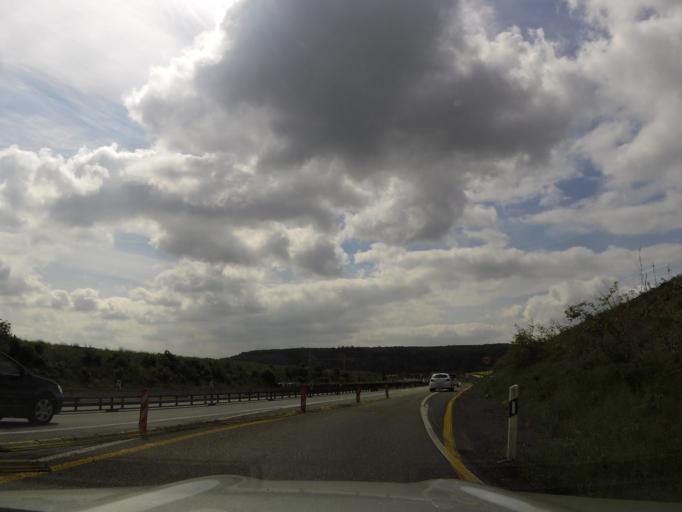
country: DE
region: Hesse
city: Allendorf an der Lahn
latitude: 50.5532
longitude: 8.5643
